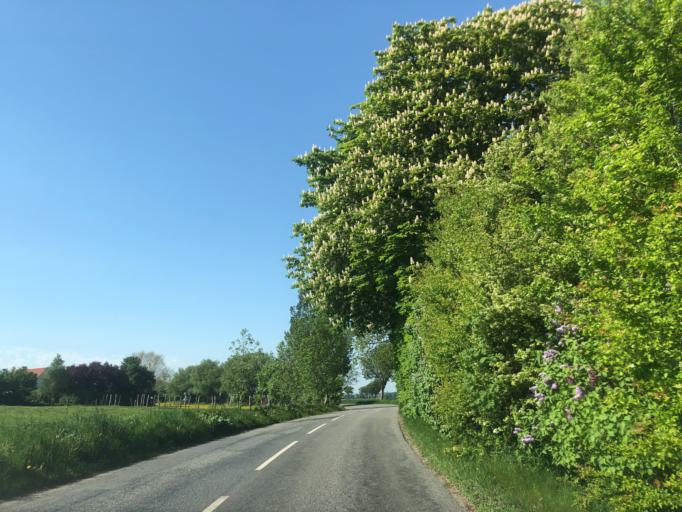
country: DK
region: Zealand
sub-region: Roskilde Kommune
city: Viby
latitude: 55.5756
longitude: 12.0299
